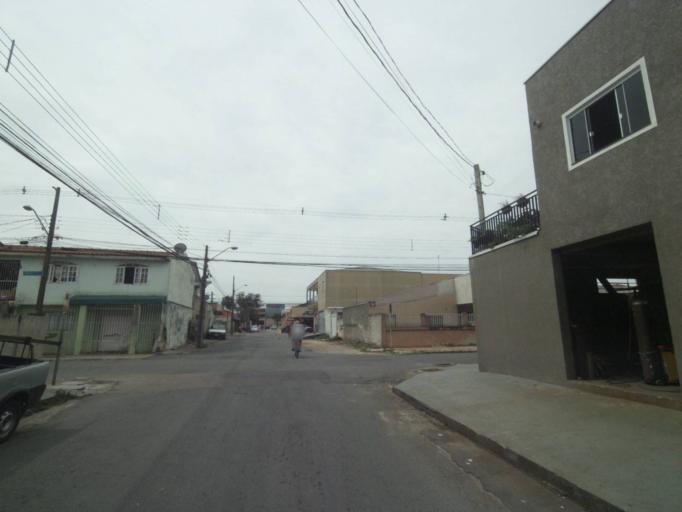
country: BR
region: Parana
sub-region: Curitiba
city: Curitiba
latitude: -25.5155
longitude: -49.3306
